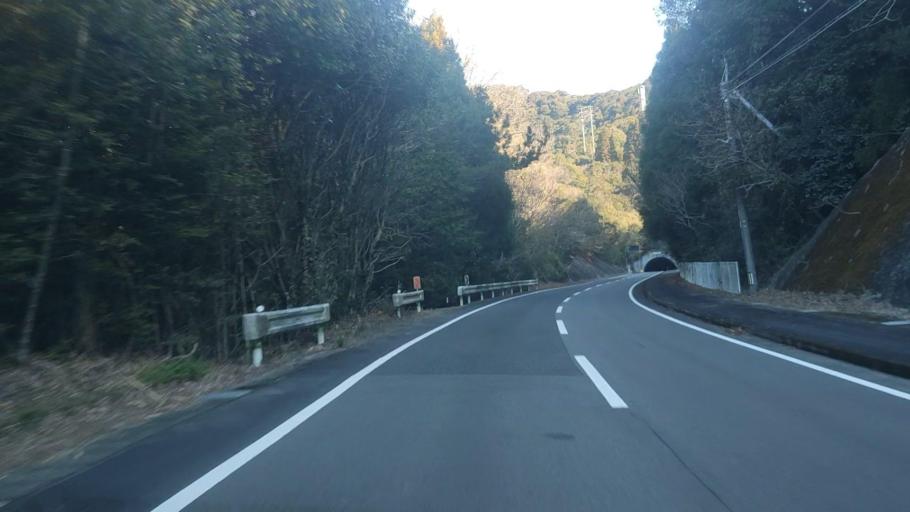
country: JP
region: Miyazaki
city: Nobeoka
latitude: 32.6690
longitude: 131.7665
